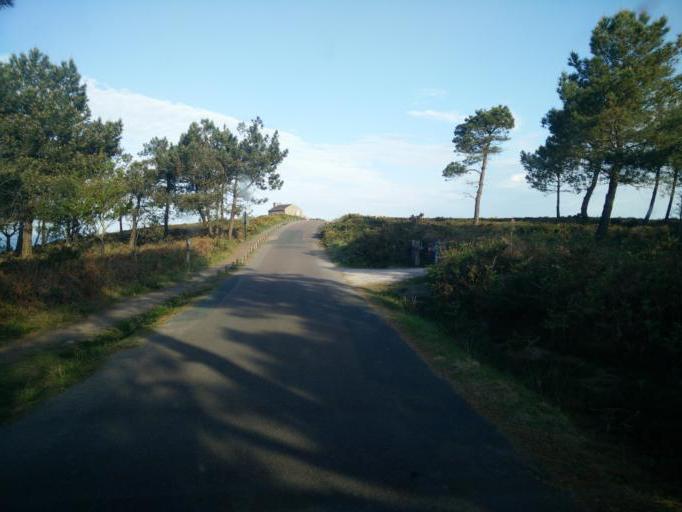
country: FR
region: Brittany
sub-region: Departement des Cotes-d'Armor
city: Erquy
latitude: 48.6393
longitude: -2.4801
